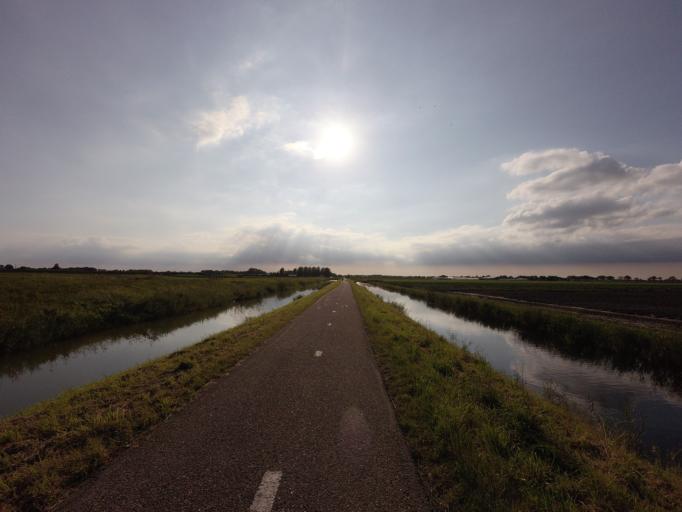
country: NL
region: North Holland
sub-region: Gemeente Hoorn
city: Hoorn
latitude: 52.6752
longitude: 5.1156
